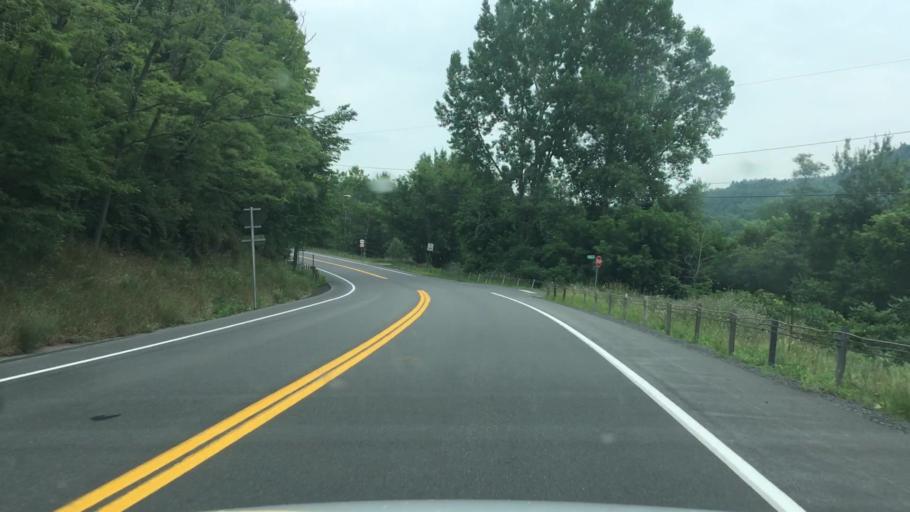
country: US
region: New York
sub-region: Essex County
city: Keeseville
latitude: 44.4675
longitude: -73.5731
